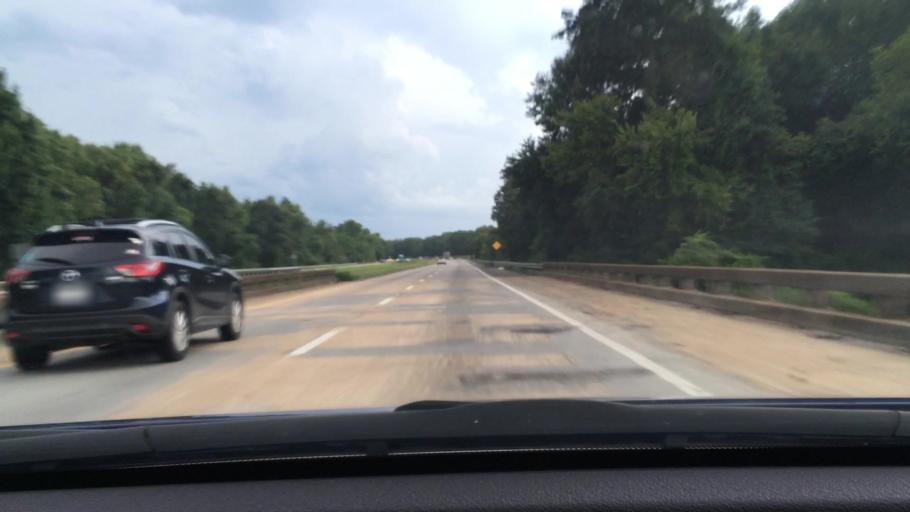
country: US
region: South Carolina
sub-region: Kershaw County
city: Camden
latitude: 34.2172
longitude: -80.6316
